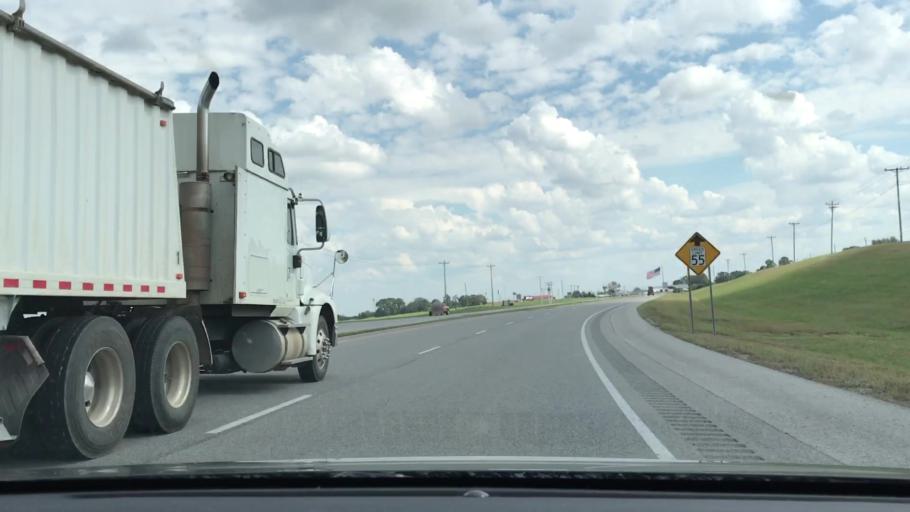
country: US
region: Kentucky
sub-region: Trigg County
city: Cadiz
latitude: 36.8763
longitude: -87.7507
